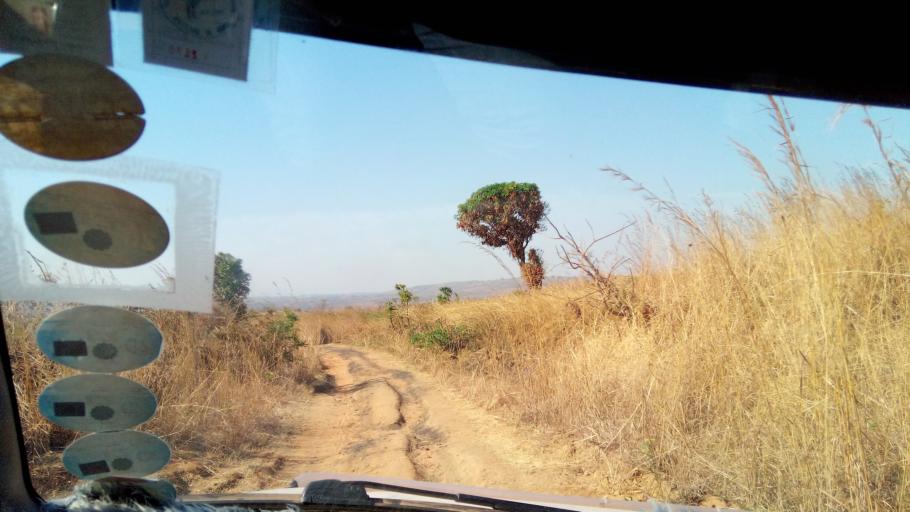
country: CD
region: Katanga
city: Kalemie
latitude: -5.9148
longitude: 29.1239
